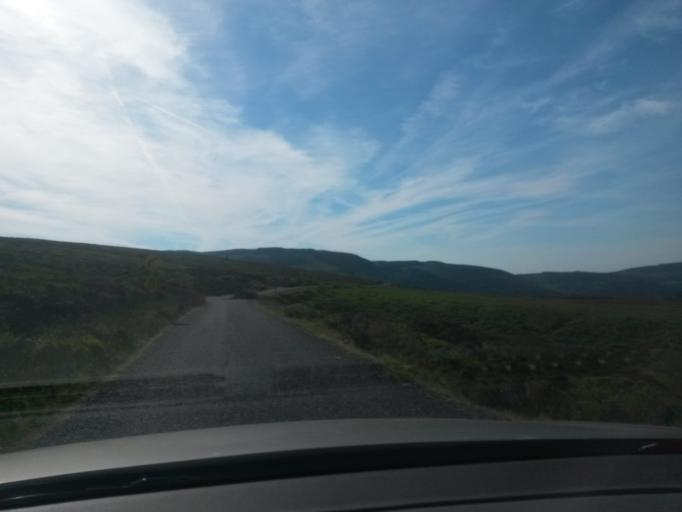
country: IE
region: Leinster
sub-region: Wicklow
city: Enniskerry
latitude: 53.1245
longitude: -6.2795
